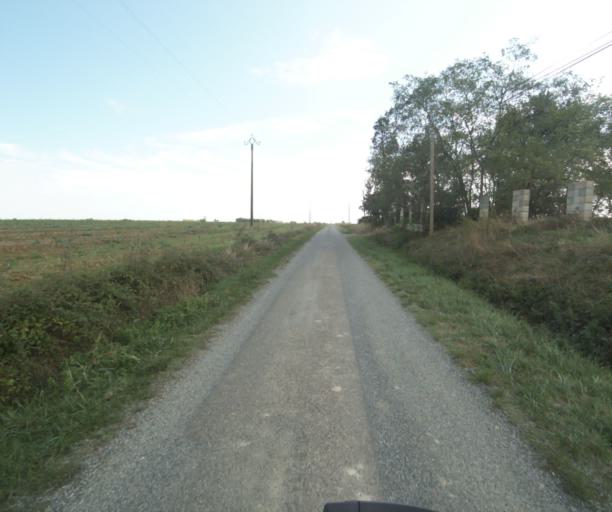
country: FR
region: Midi-Pyrenees
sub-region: Departement du Tarn-et-Garonne
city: Verdun-sur-Garonne
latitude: 43.8471
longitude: 1.1696
